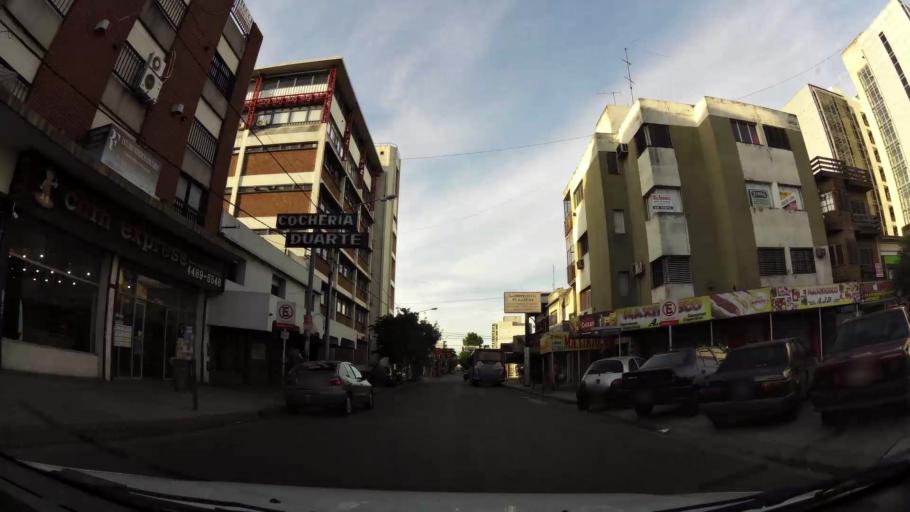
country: AR
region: Buenos Aires
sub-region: Partido de Moron
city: Moron
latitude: -34.6470
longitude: -58.6211
